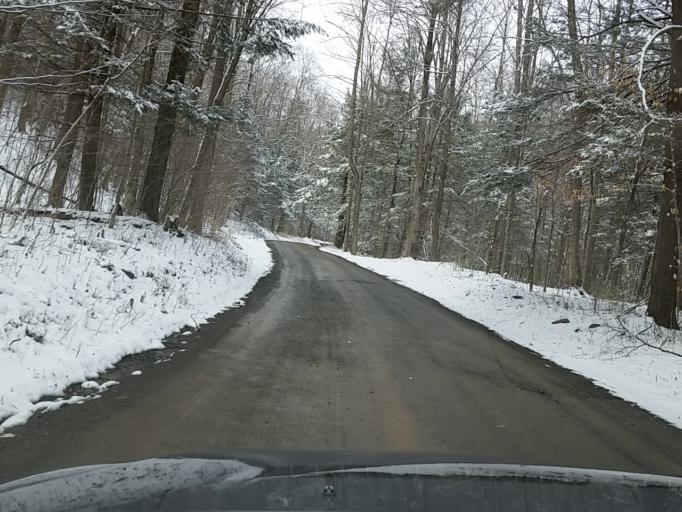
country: US
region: Pennsylvania
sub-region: Sullivan County
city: Laporte
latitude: 41.3121
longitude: -76.4426
